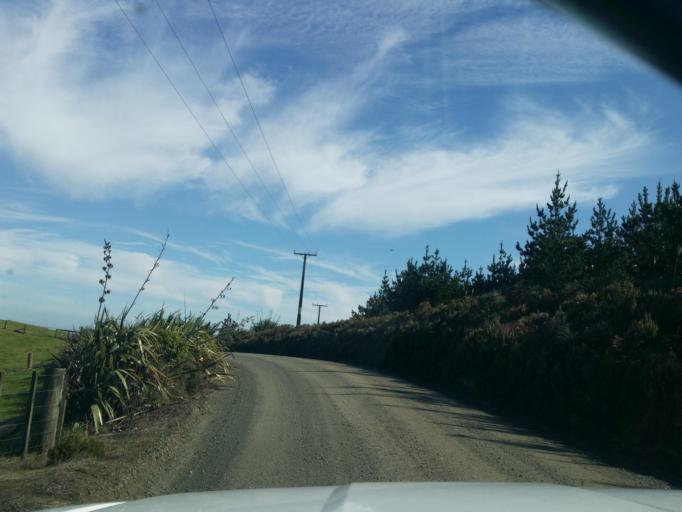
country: NZ
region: Northland
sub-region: Kaipara District
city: Dargaville
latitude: -35.8867
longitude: 173.7202
